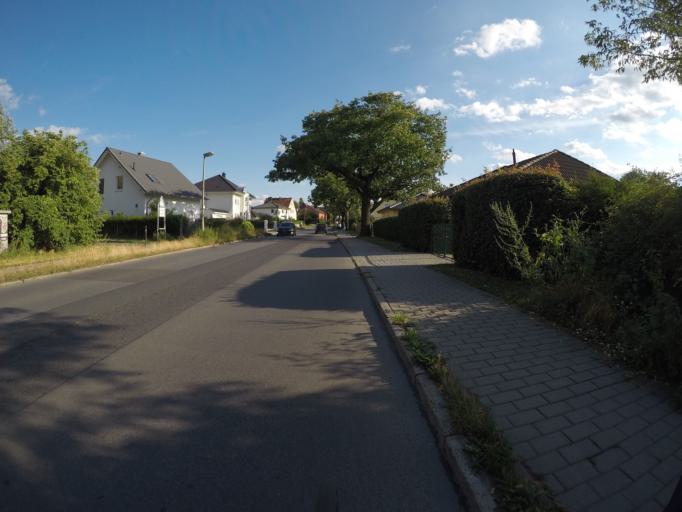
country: DE
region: Berlin
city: Wartenberg
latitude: 52.5773
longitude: 13.5190
